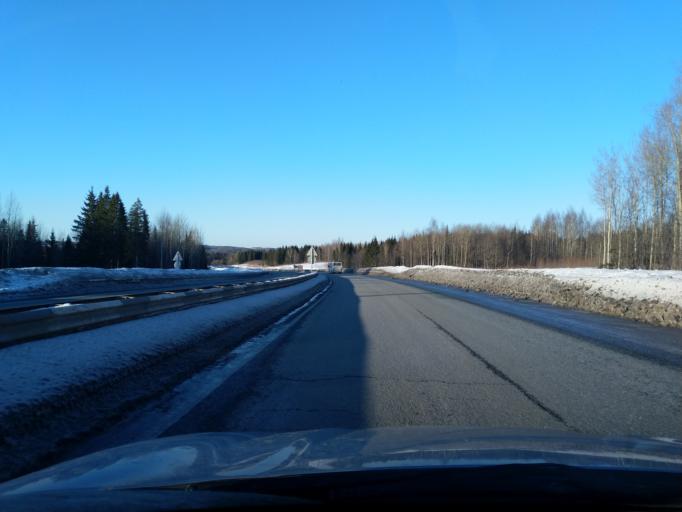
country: RU
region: Perm
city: Polazna
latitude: 58.2994
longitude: 56.4839
